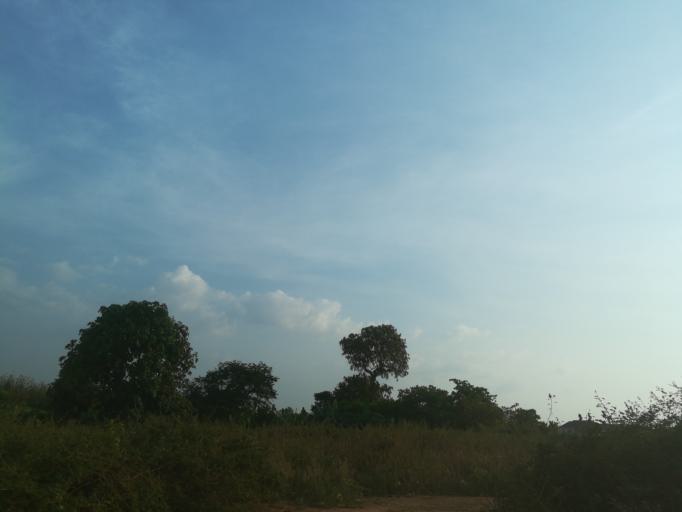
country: NG
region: Abuja Federal Capital Territory
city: Abuja
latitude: 9.1026
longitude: 7.3739
